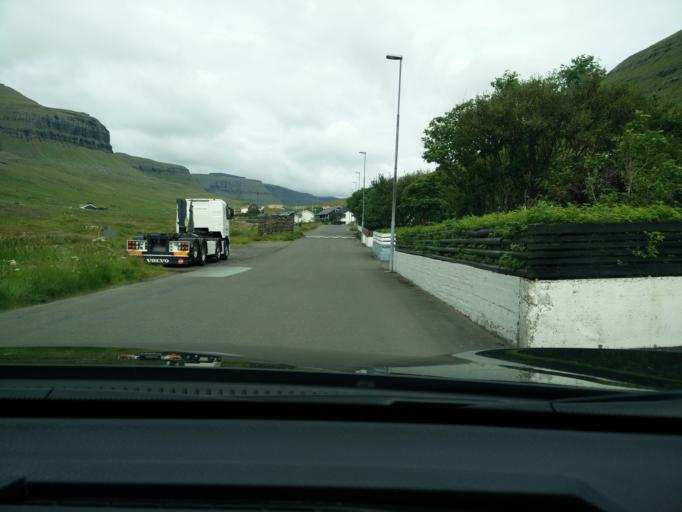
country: FO
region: Eysturoy
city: Eystur
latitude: 62.2011
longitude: -6.7481
